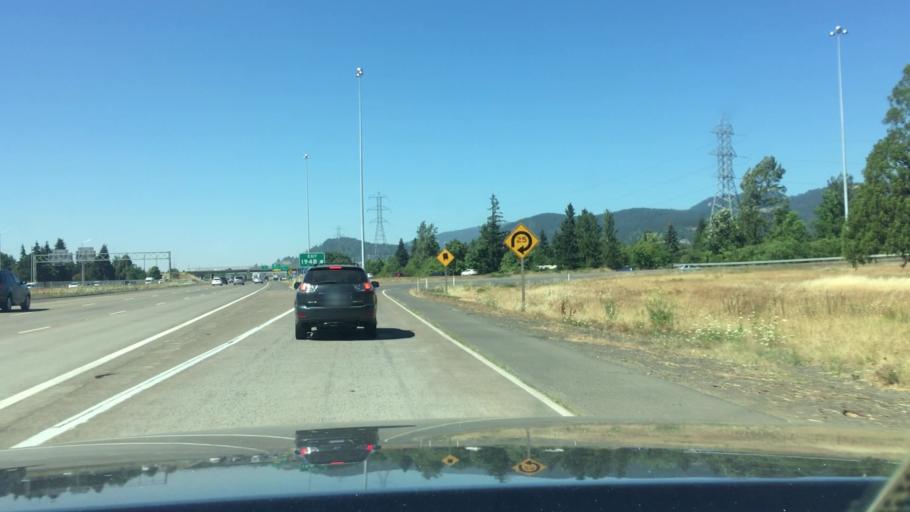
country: US
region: Oregon
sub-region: Lane County
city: Springfield
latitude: 44.0640
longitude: -123.0488
